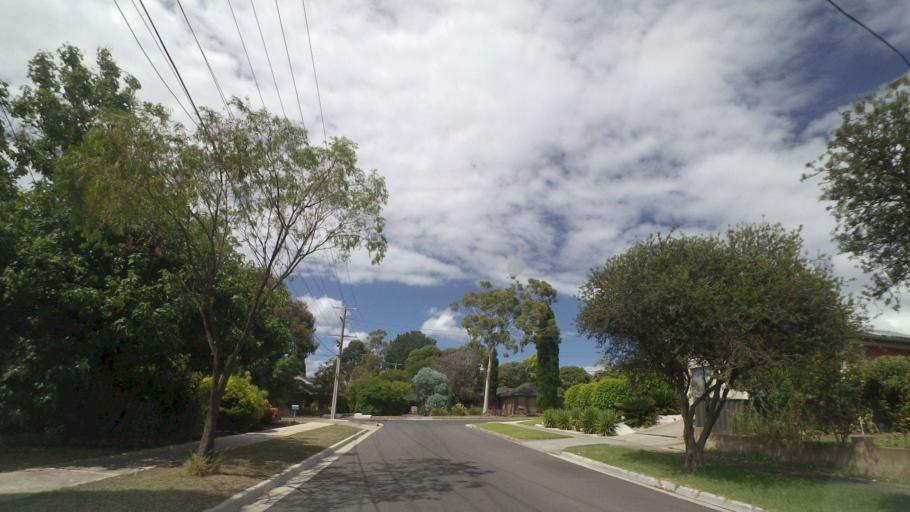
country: AU
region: Victoria
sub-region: Knox
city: Wantirna South
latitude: -37.8825
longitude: 145.2215
